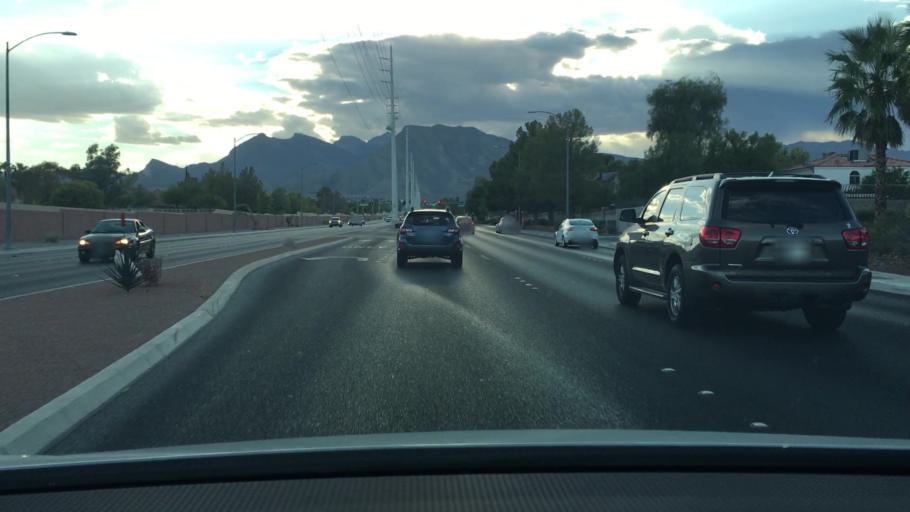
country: US
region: Nevada
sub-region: Clark County
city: Summerlin South
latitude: 36.2187
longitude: -115.2850
